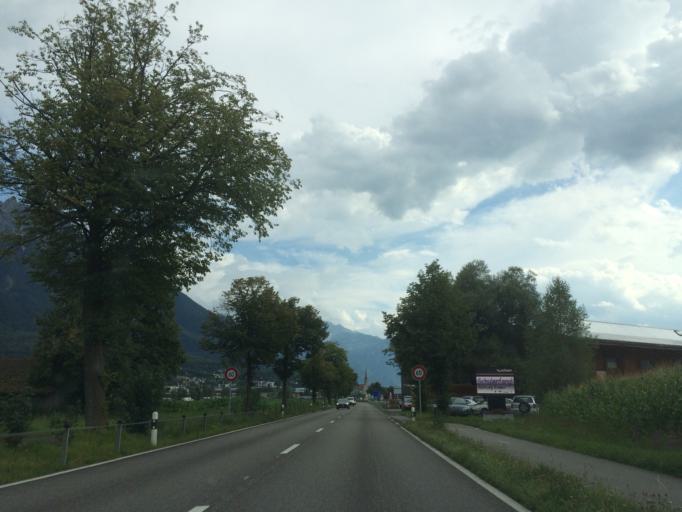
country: LI
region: Schaan
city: Schaan
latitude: 47.1811
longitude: 9.5071
